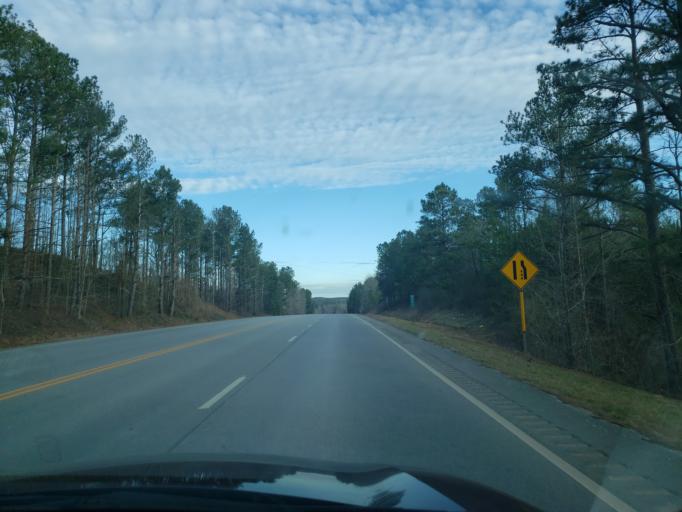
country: US
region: Alabama
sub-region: Randolph County
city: Wedowee
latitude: 33.3934
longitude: -85.5255
